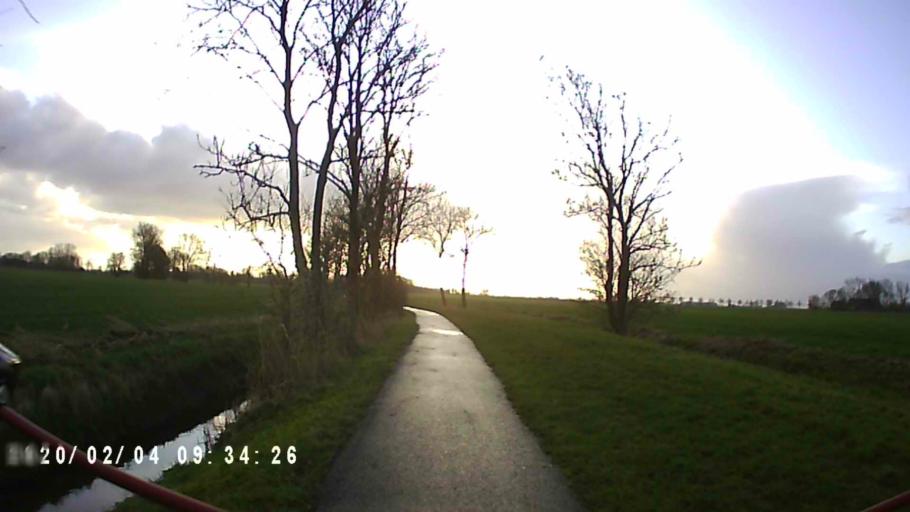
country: NL
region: Groningen
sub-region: Gemeente Zuidhorn
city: Aduard
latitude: 53.3094
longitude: 6.4554
